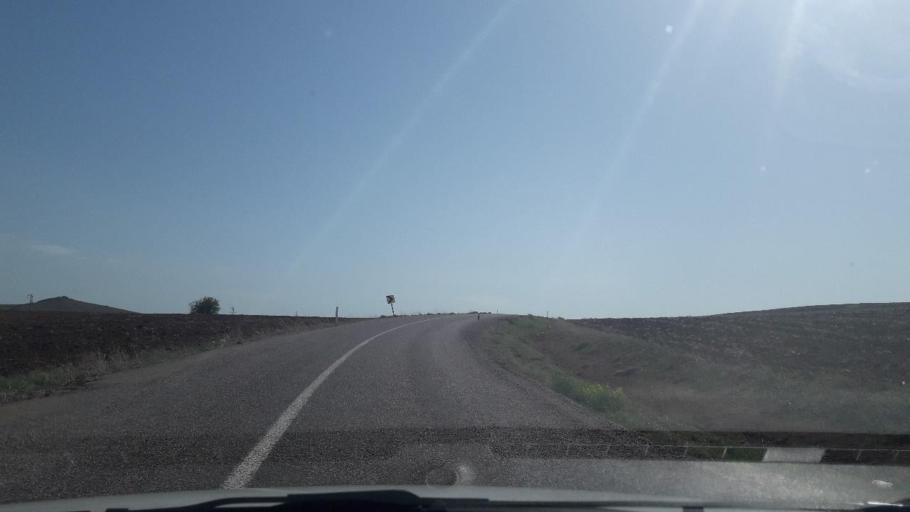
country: TR
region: Sivas
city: Alacahan
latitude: 39.0773
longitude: 37.5529
